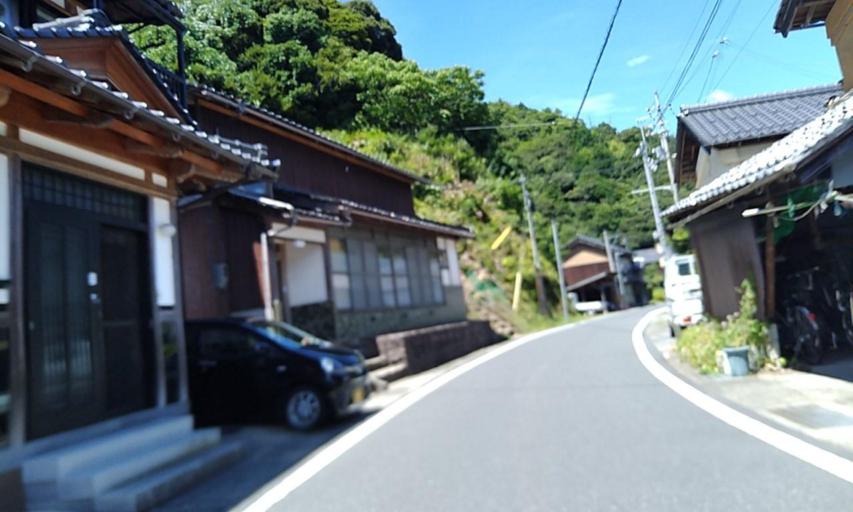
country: JP
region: Kyoto
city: Miyazu
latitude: 35.6701
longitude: 135.2744
